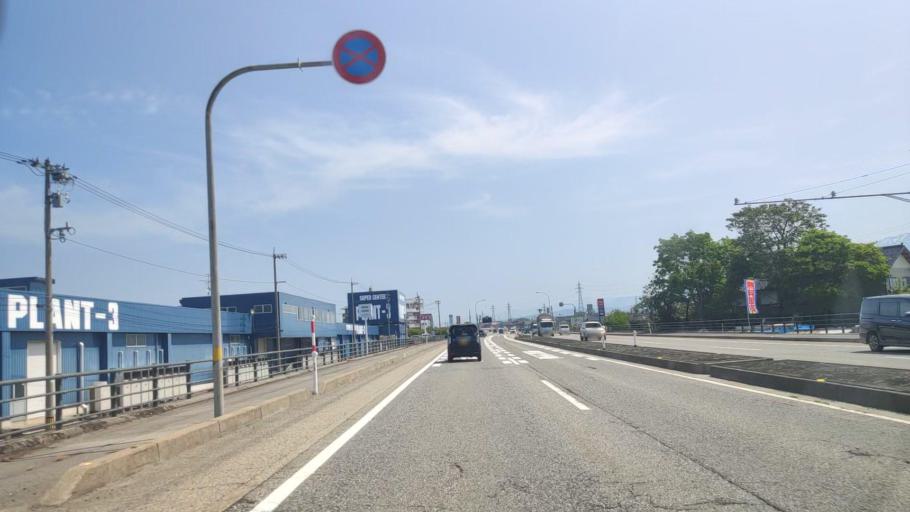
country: JP
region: Toyama
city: Namerikawa
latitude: 36.7498
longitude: 137.3517
